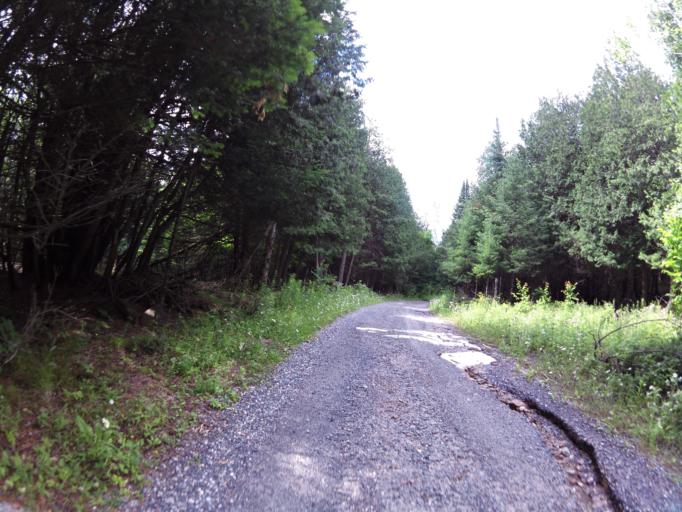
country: CA
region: Ontario
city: Perth
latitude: 45.0685
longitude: -76.4753
